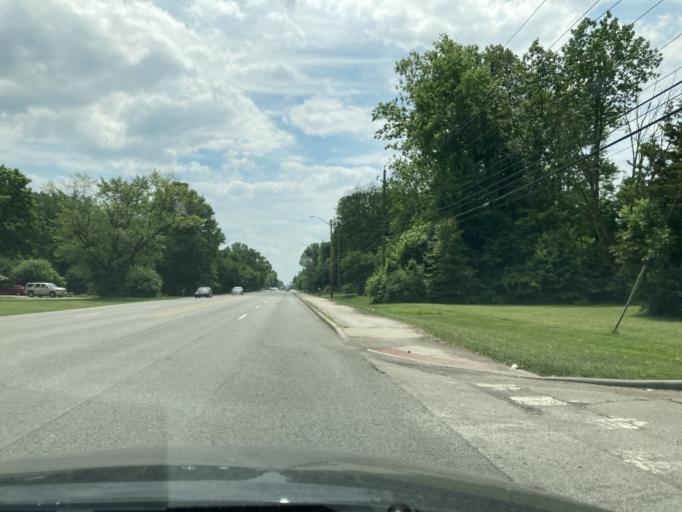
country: US
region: Indiana
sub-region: Marion County
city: Meridian Hills
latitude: 39.8771
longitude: -86.2062
